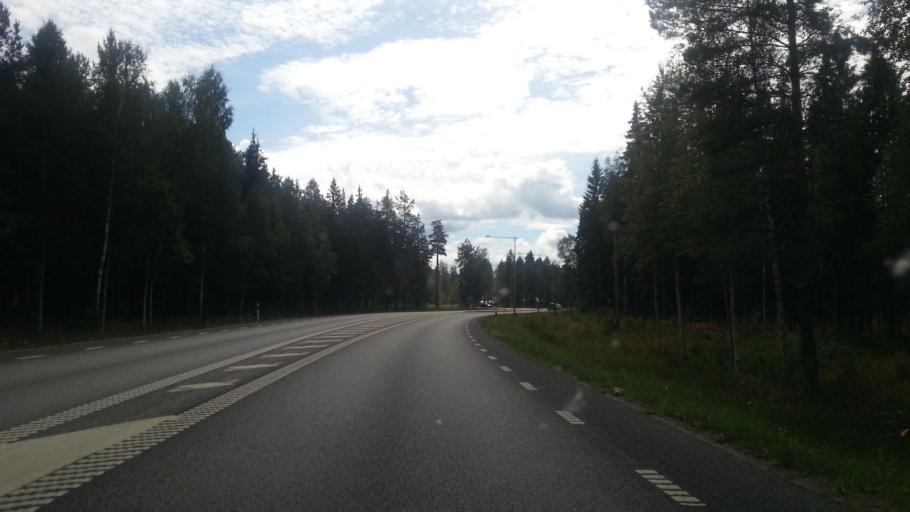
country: SE
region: OErebro
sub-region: Lindesbergs Kommun
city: Lindesberg
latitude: 59.6199
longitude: 15.1889
